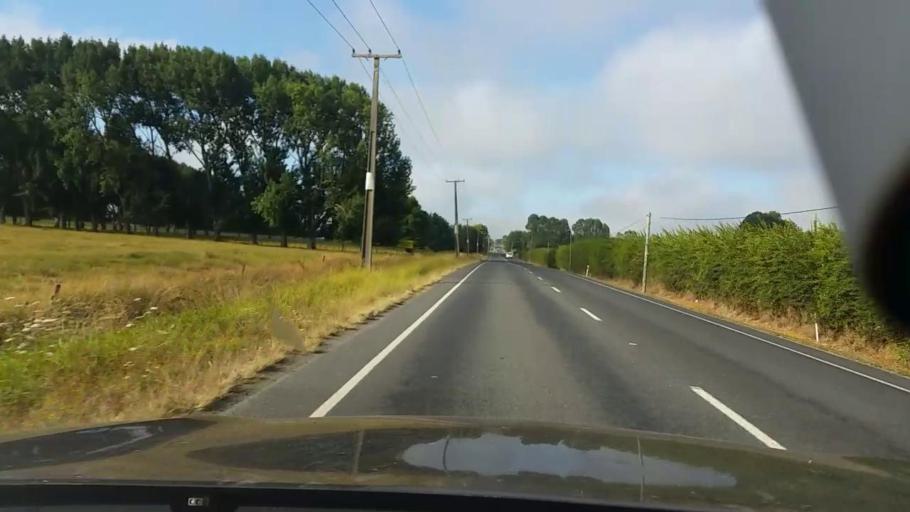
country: NZ
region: Waikato
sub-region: Hamilton City
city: Hamilton
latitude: -37.6012
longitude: 175.3523
